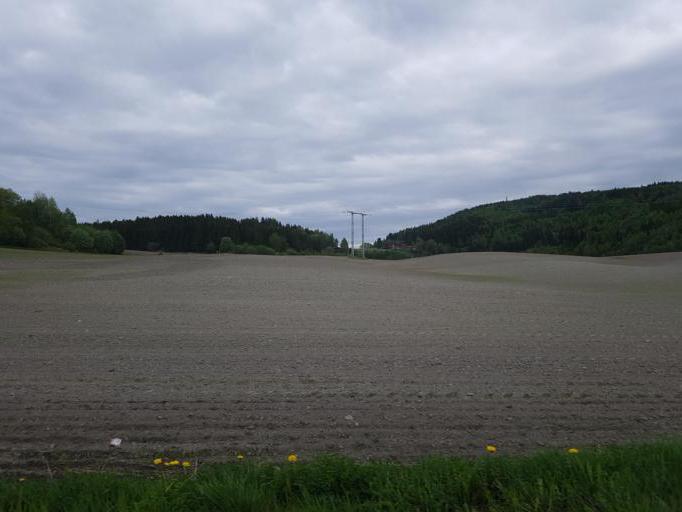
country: NO
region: Nord-Trondelag
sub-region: Levanger
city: Levanger
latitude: 63.7190
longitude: 11.2558
